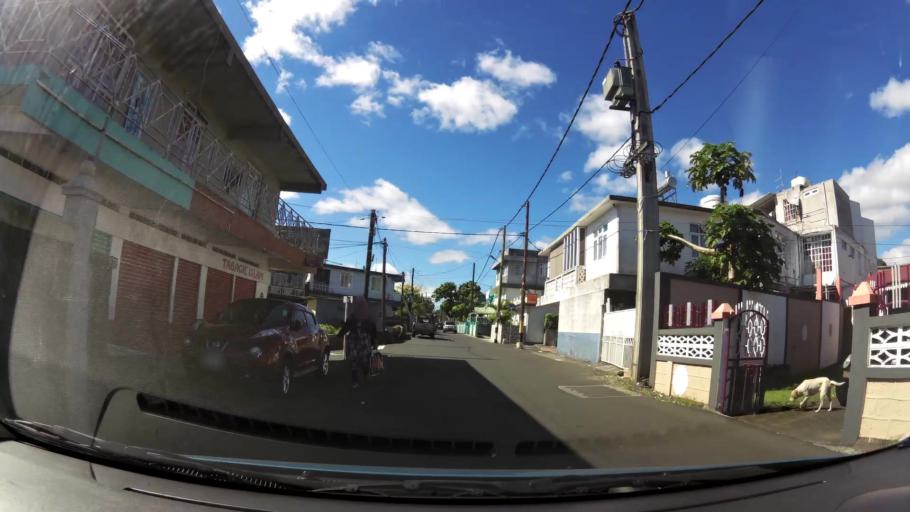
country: MU
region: Plaines Wilhems
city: Vacoas
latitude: -20.3083
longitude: 57.4839
